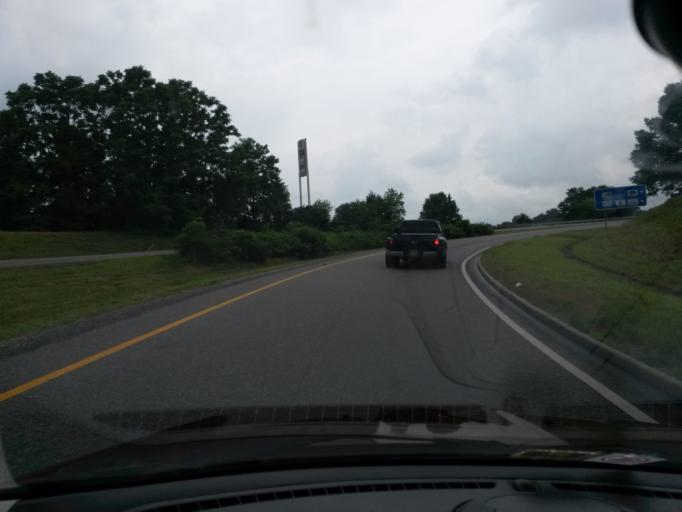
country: US
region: Virginia
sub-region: Augusta County
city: Lyndhurst
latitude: 38.0595
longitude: -78.9407
